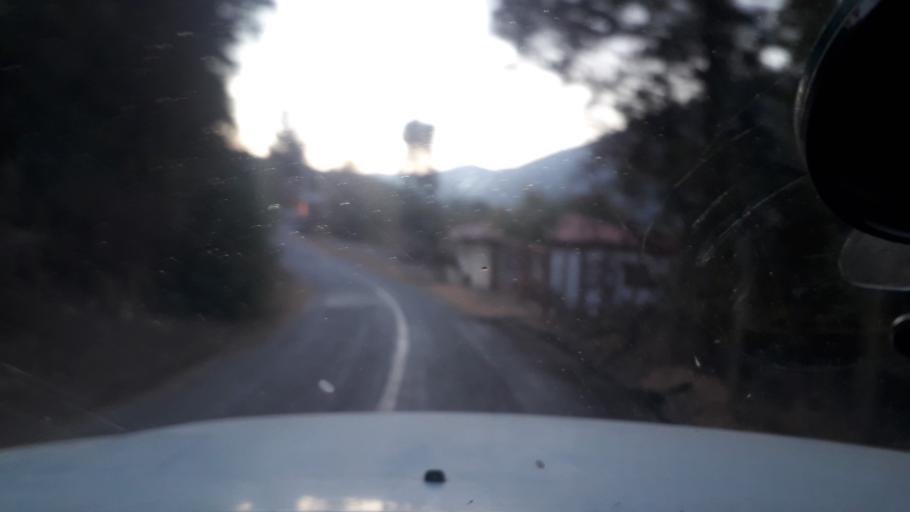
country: CL
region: Valparaiso
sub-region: Provincia de Marga Marga
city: Limache
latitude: -33.1790
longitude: -71.1160
